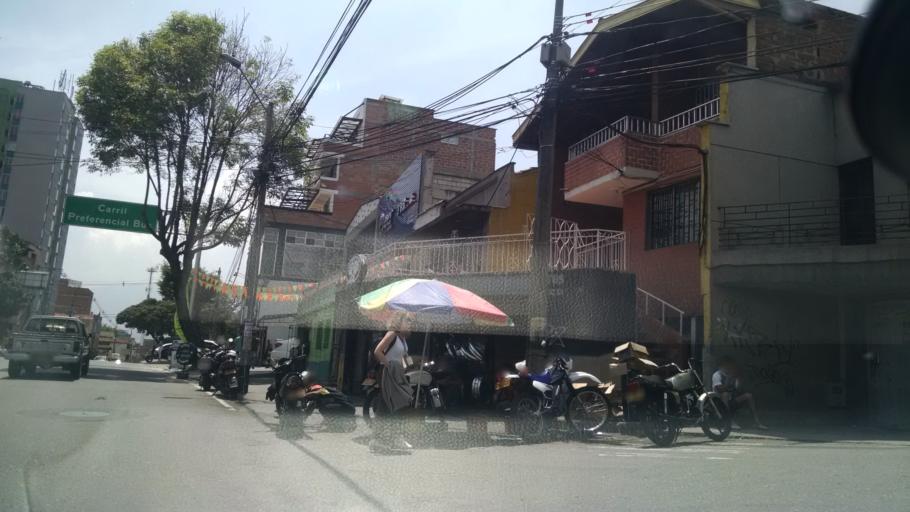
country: CO
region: Antioquia
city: Medellin
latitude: 6.2551
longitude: -75.6123
